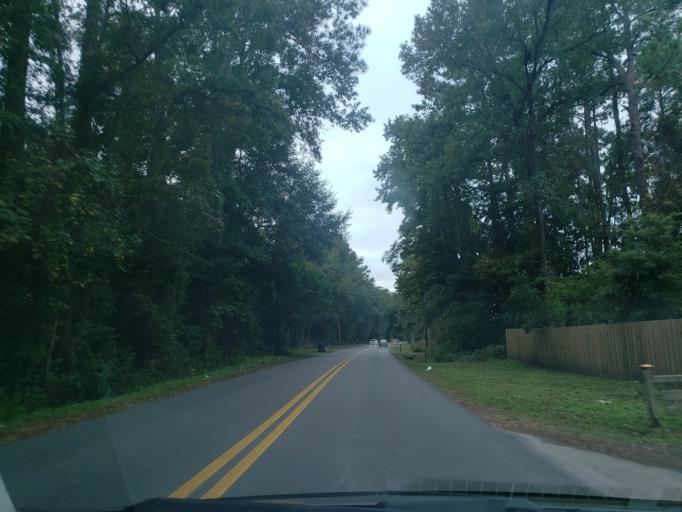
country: US
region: Georgia
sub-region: Chatham County
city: Montgomery
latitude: 31.9537
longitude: -81.1064
